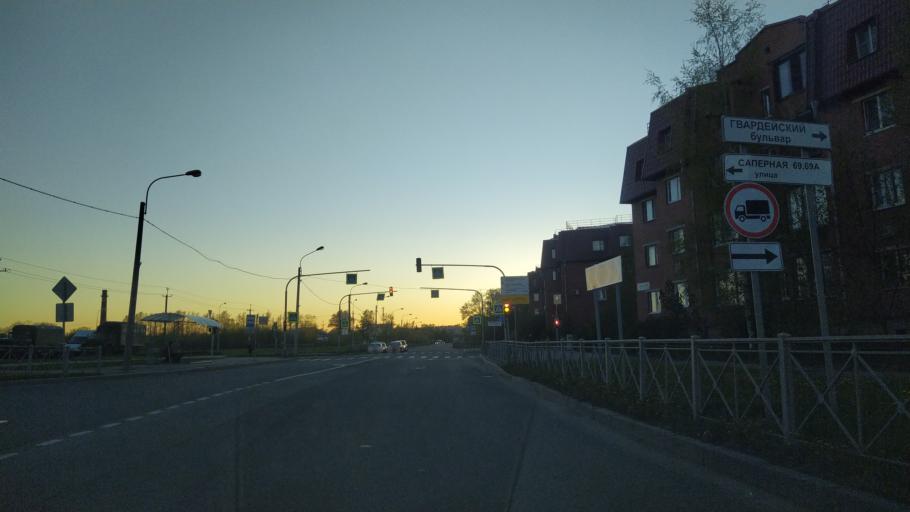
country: RU
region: St.-Petersburg
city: Pushkin
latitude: 59.7007
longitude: 30.3817
